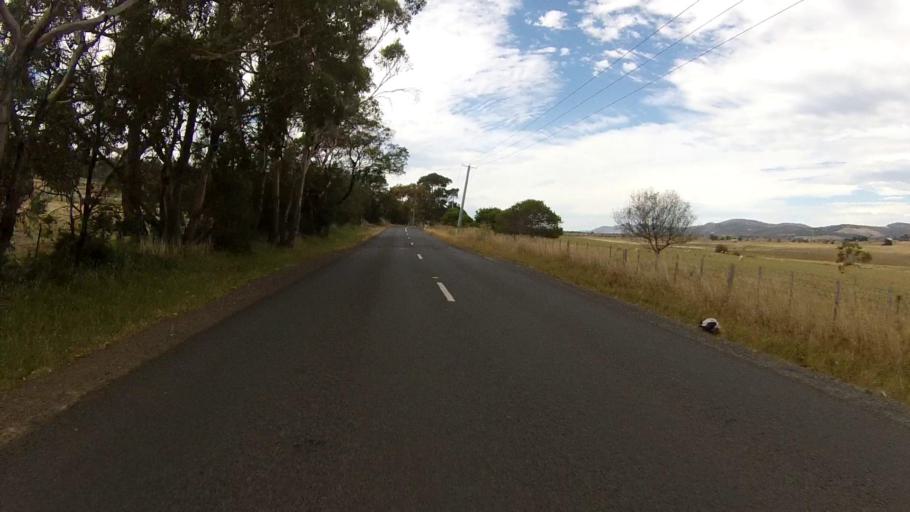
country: AU
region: Tasmania
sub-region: Clarence
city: Cambridge
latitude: -42.7231
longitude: 147.3956
